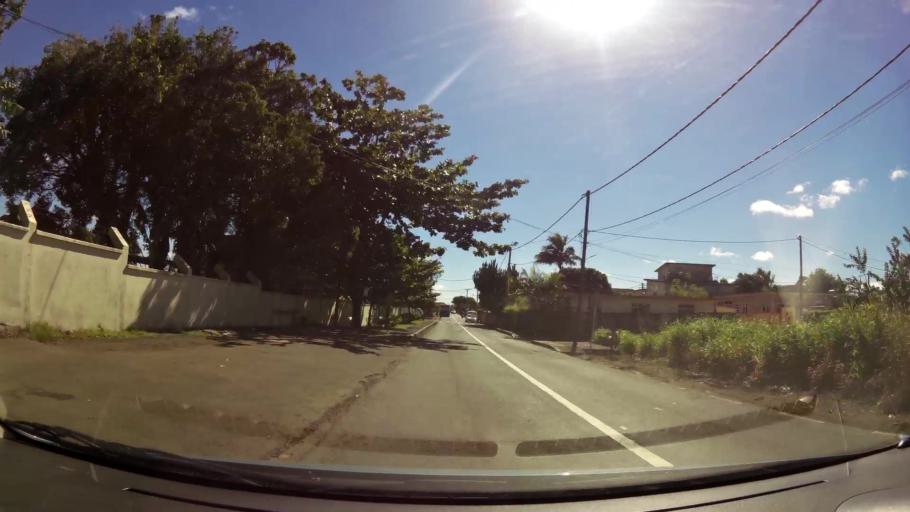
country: MU
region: Plaines Wilhems
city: Curepipe
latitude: -20.3379
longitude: 57.4916
